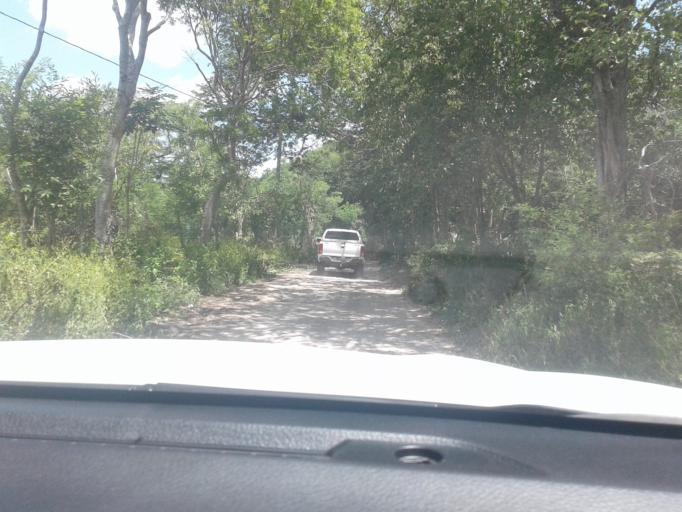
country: NI
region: Matagalpa
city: Terrabona
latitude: 12.5616
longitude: -86.0368
